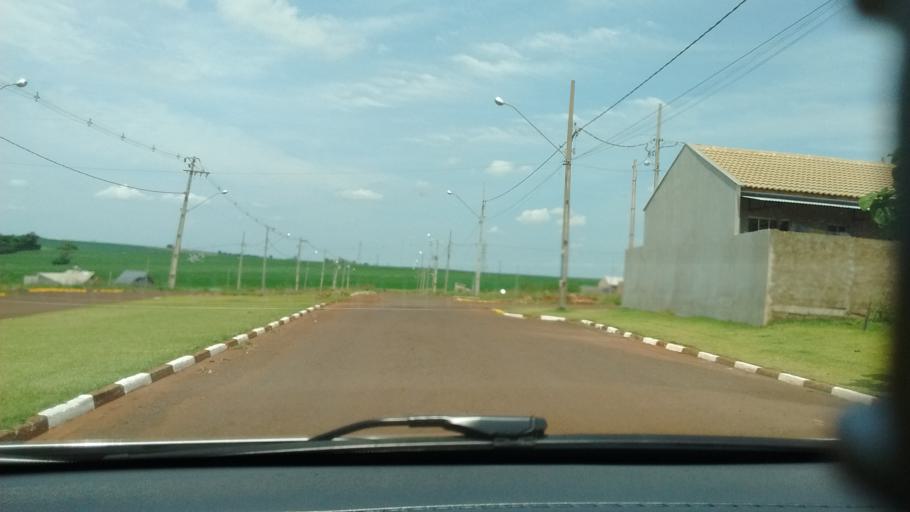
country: BR
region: Parana
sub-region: Corbelia
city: Corbelia
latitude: -24.5498
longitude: -52.9771
